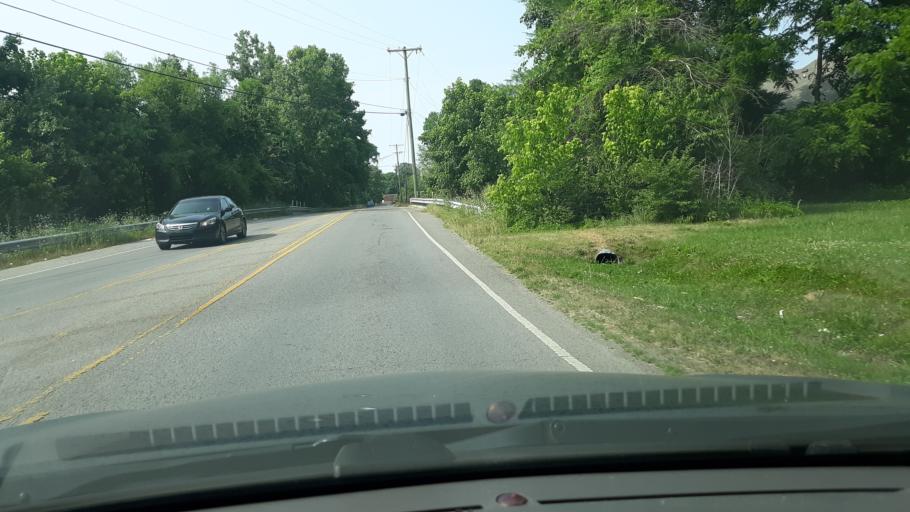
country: US
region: Tennessee
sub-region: Davidson County
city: Lakewood
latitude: 36.1783
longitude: -86.6137
